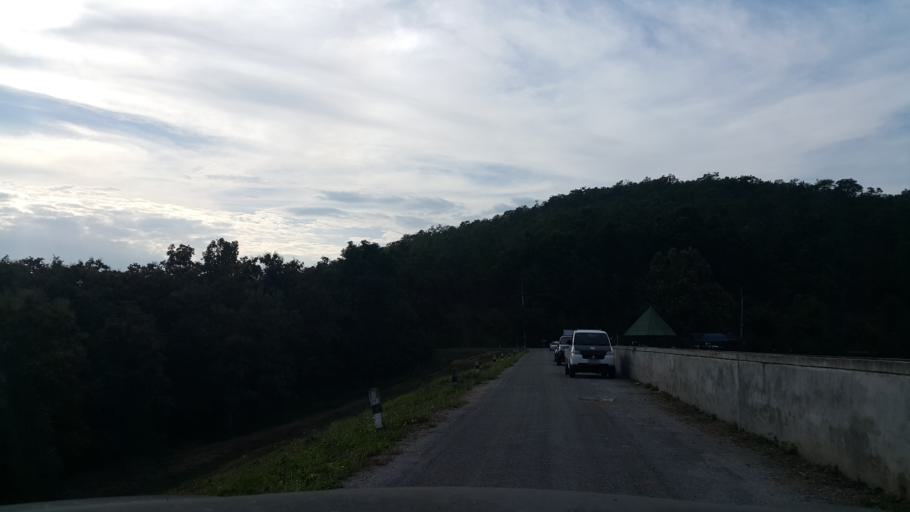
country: TH
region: Chiang Mai
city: San Sai
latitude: 18.9373
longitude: 99.0621
